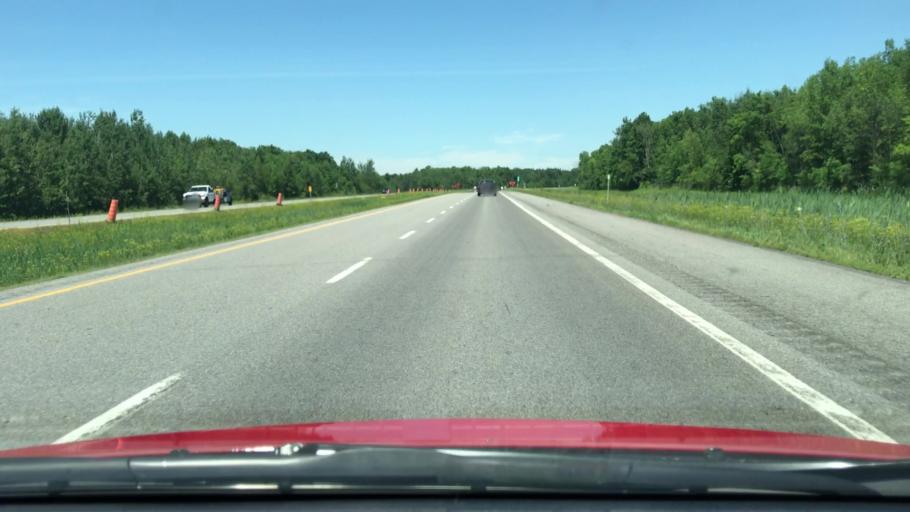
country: CA
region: Quebec
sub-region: Monteregie
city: Napierville
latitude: 45.1594
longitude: -73.4676
